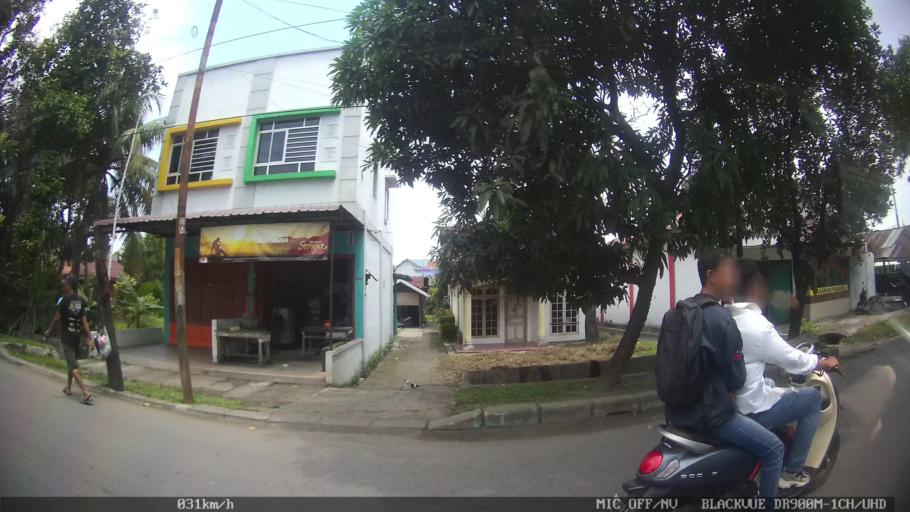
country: ID
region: North Sumatra
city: Labuhan Deli
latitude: 3.6586
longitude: 98.6655
